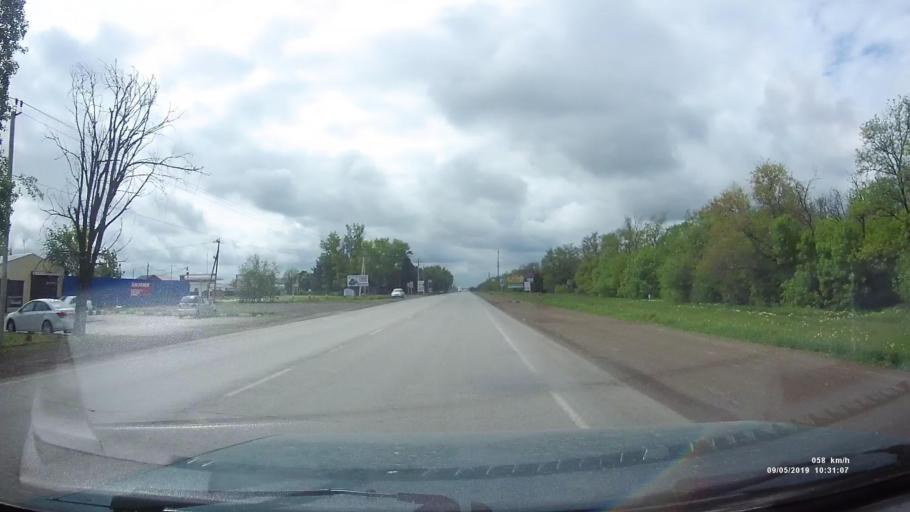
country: RU
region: Rostov
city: Azov
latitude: 47.0846
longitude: 39.4283
